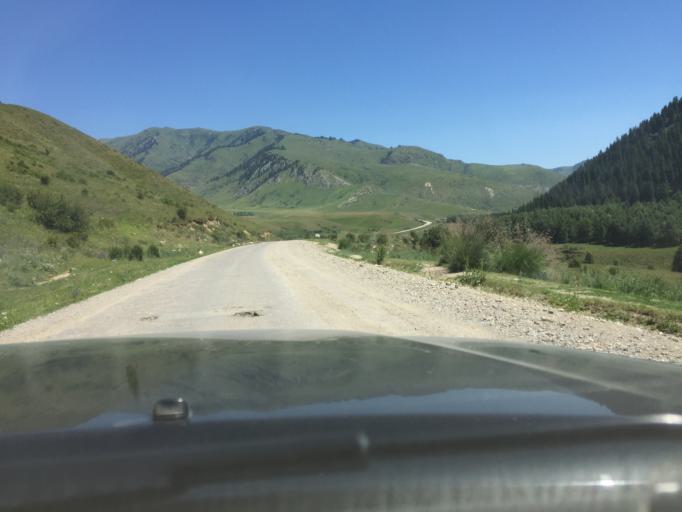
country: KG
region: Ysyk-Koel
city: Teploklyuchenka
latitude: 42.7302
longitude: 78.8233
